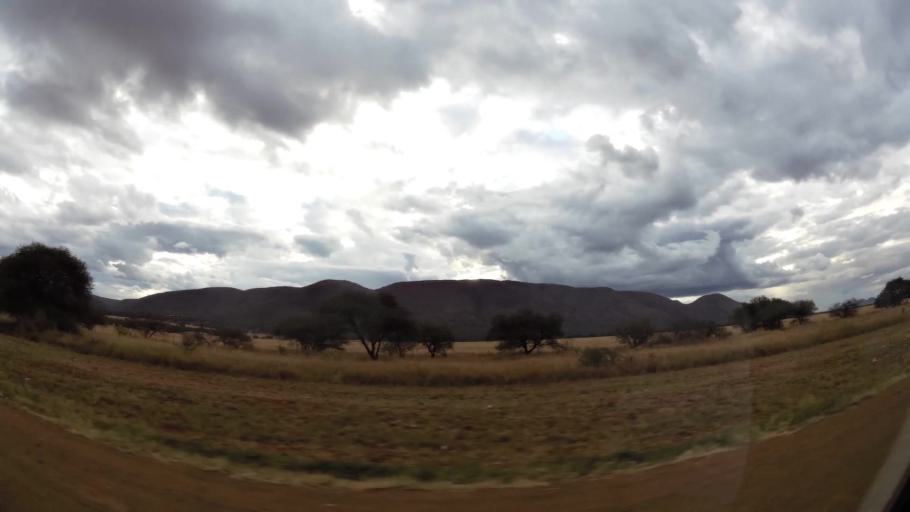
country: ZA
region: Limpopo
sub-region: Waterberg District Municipality
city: Mokopane
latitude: -24.2558
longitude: 28.9880
